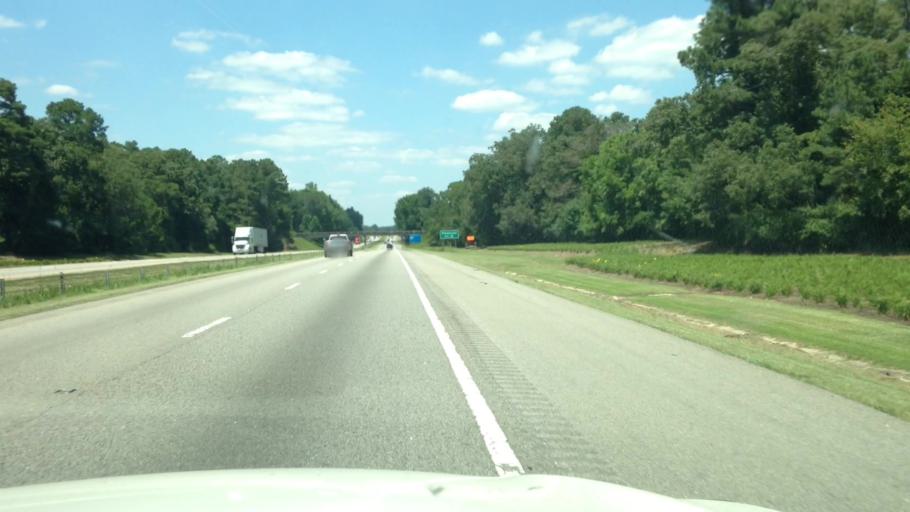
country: US
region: North Carolina
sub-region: Robeson County
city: Saint Pauls
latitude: 34.7965
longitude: -78.9924
